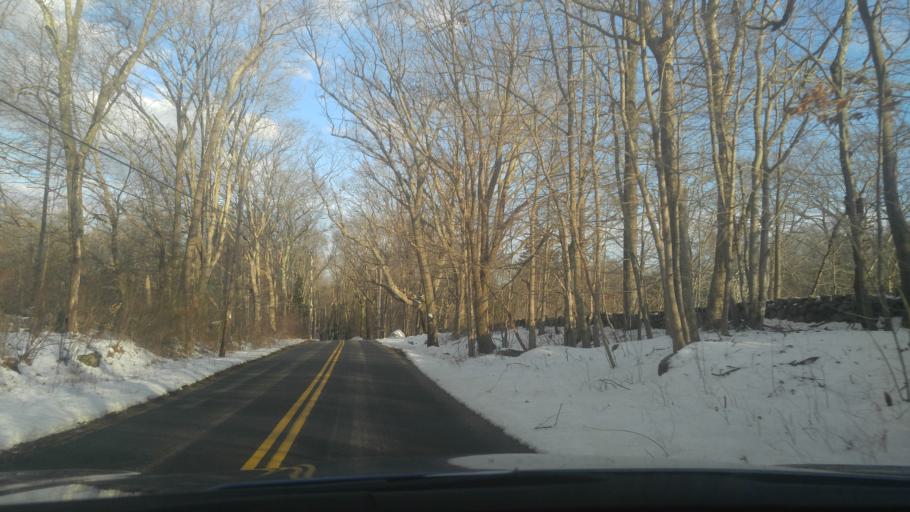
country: US
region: Rhode Island
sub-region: Kent County
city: Coventry
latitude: 41.7164
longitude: -71.6974
